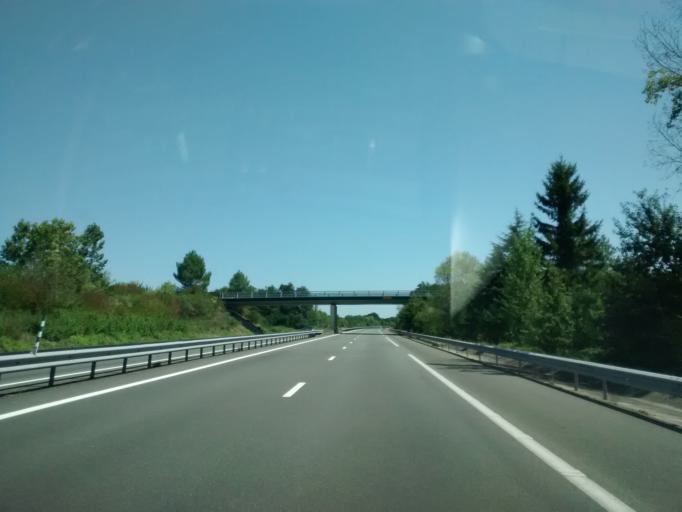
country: FR
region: Aquitaine
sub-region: Departement de la Gironde
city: Saint-Medard-de-Guizieres
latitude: 45.0077
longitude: -0.0531
